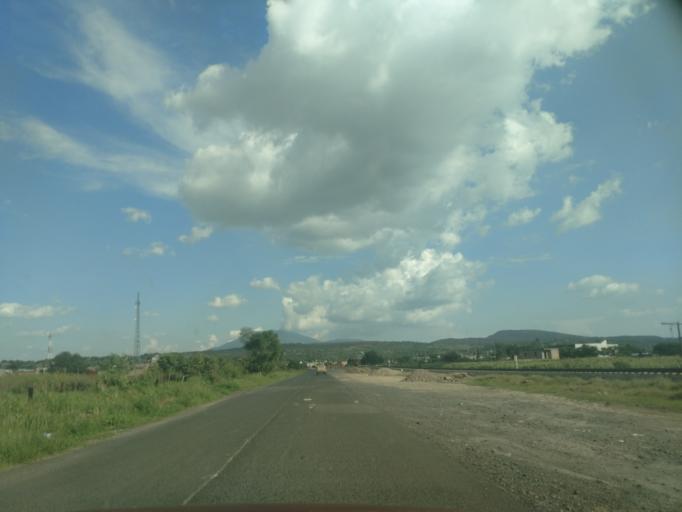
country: MX
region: Jalisco
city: Antonio Escobedo
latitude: 20.9076
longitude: -103.9872
